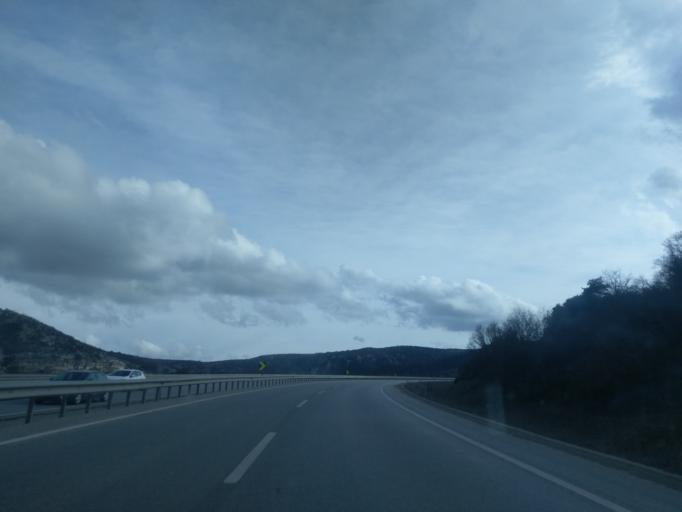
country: TR
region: Kuetahya
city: Sabuncu
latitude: 39.5625
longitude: 30.0756
